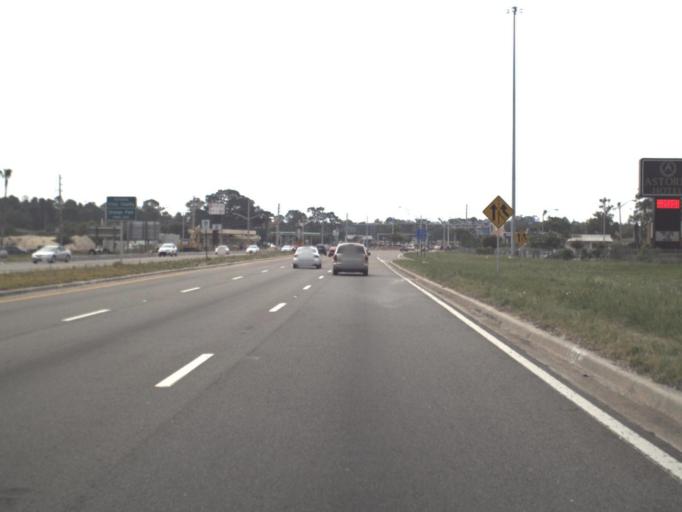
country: US
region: Florida
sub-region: Clay County
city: Orange Park
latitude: 30.1903
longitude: -81.7045
